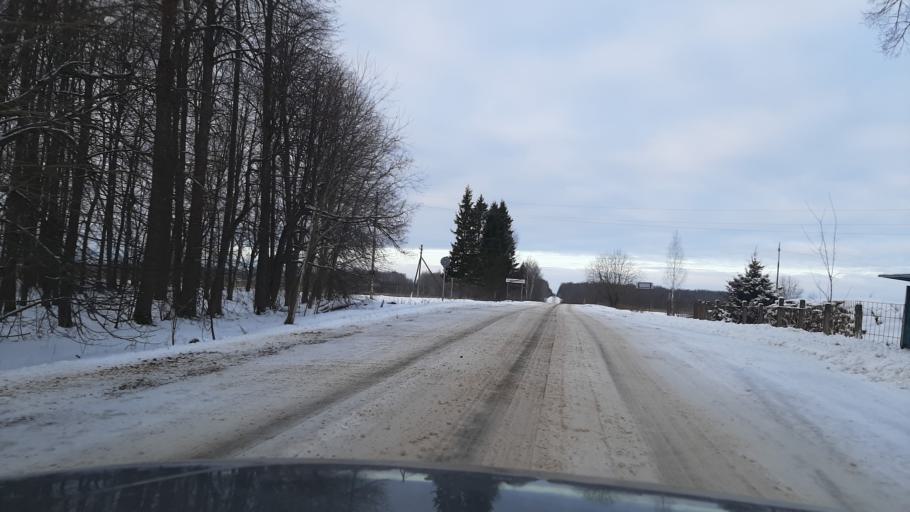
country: RU
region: Kostroma
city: Kosmynino
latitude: 57.4814
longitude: 40.7689
